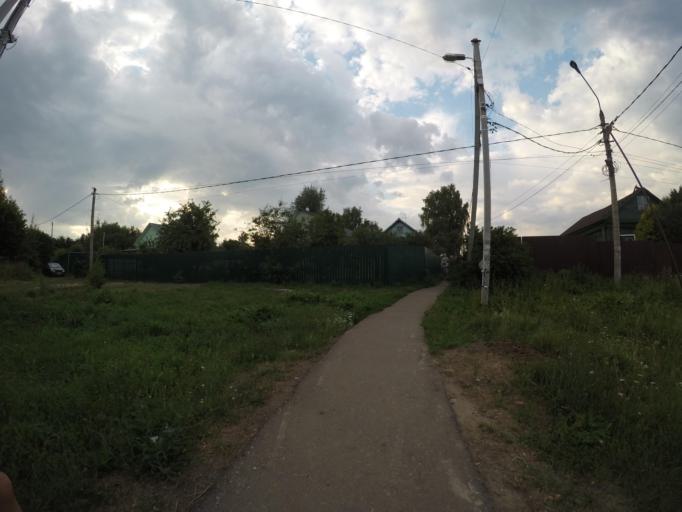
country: RU
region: Moskovskaya
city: Rechitsy
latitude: 55.5974
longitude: 38.5053
